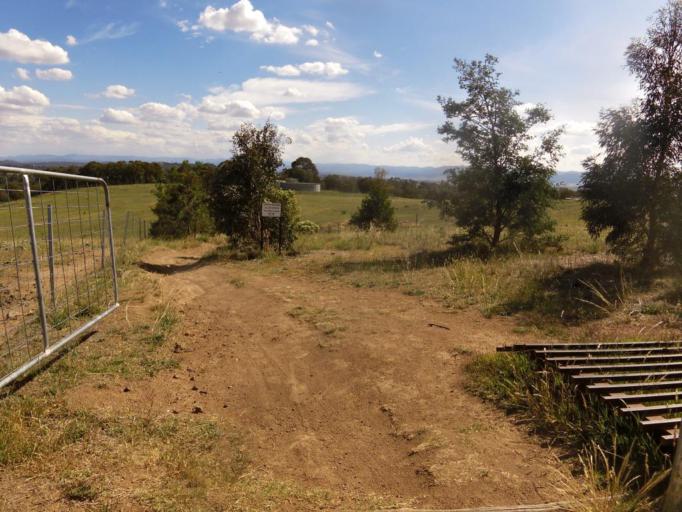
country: AU
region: Australian Capital Territory
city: Belconnen
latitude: -35.1631
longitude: 149.0737
